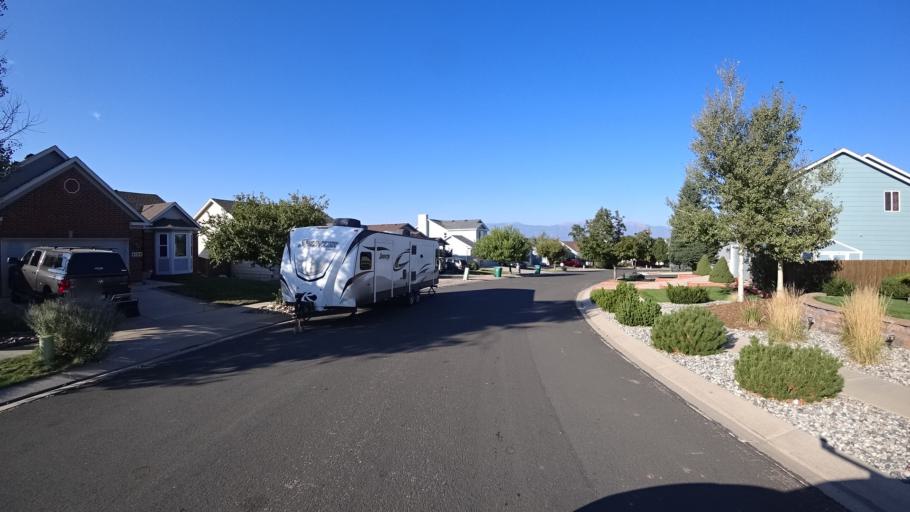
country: US
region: Colorado
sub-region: El Paso County
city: Cimarron Hills
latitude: 38.8902
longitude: -104.6998
